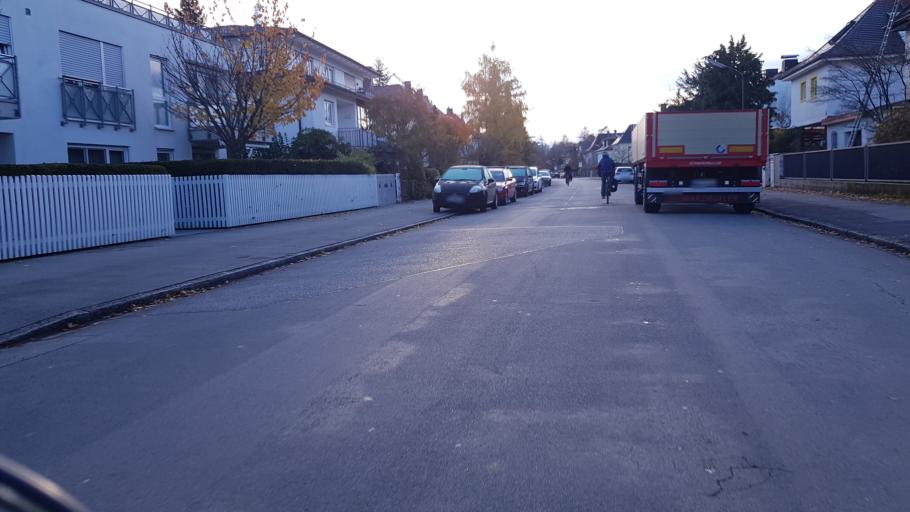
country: DE
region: Bavaria
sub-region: Upper Bavaria
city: Munich
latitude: 48.0923
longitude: 11.5711
